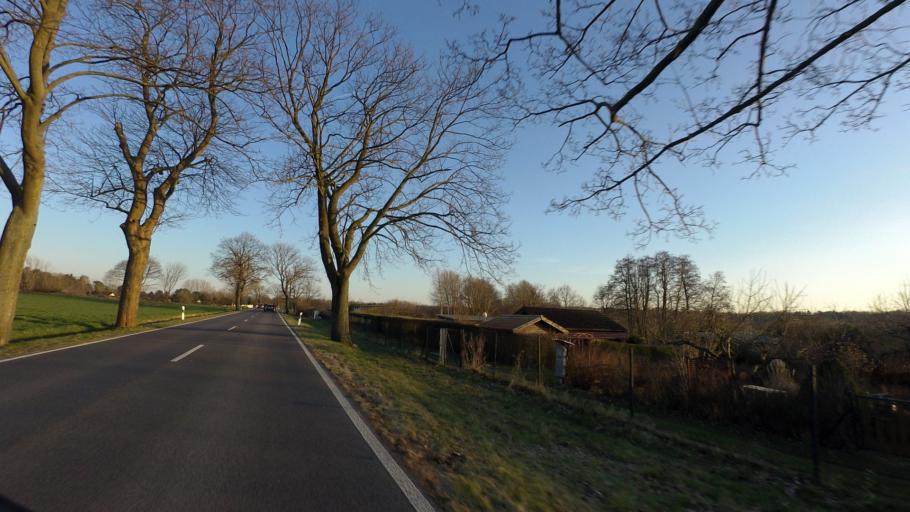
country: DE
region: Berlin
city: Hellersdorf
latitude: 52.5655
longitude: 13.6264
